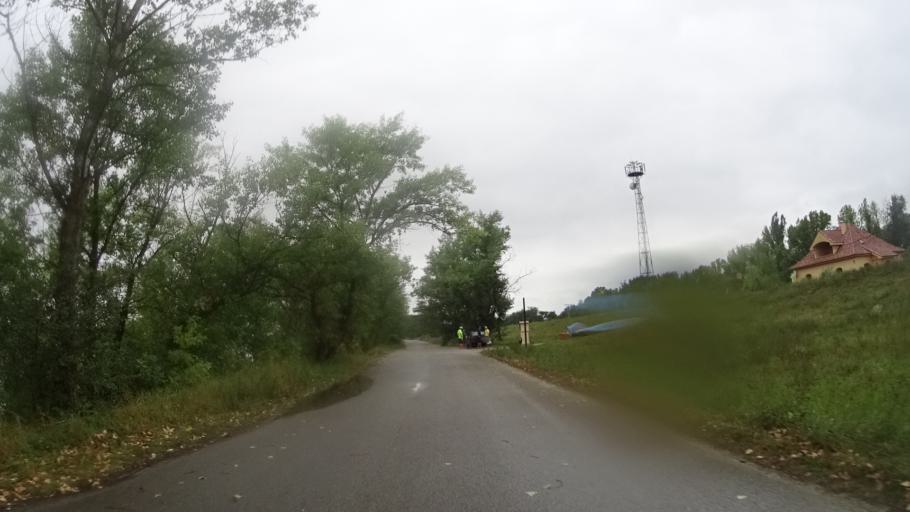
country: HU
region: Komarom-Esztergom
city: Sutto
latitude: 47.7652
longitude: 18.4707
